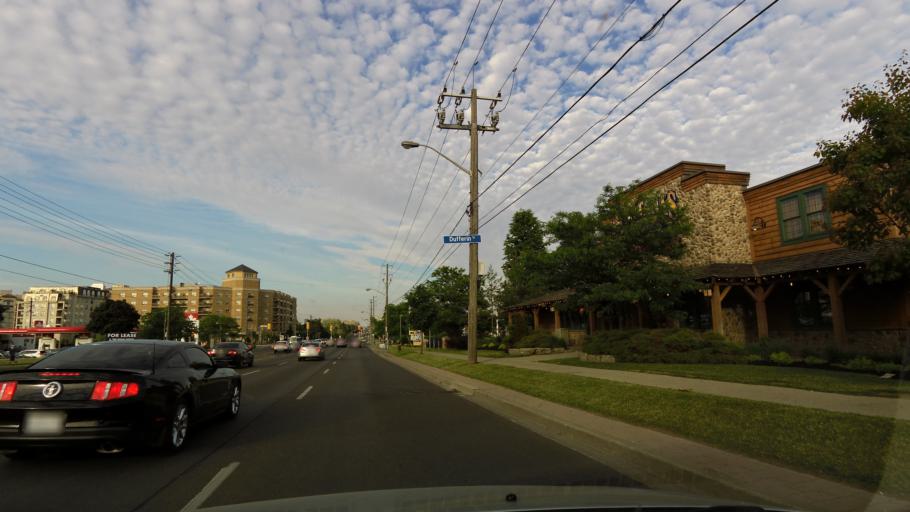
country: CA
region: Ontario
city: Concord
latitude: 43.7868
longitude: -79.4718
